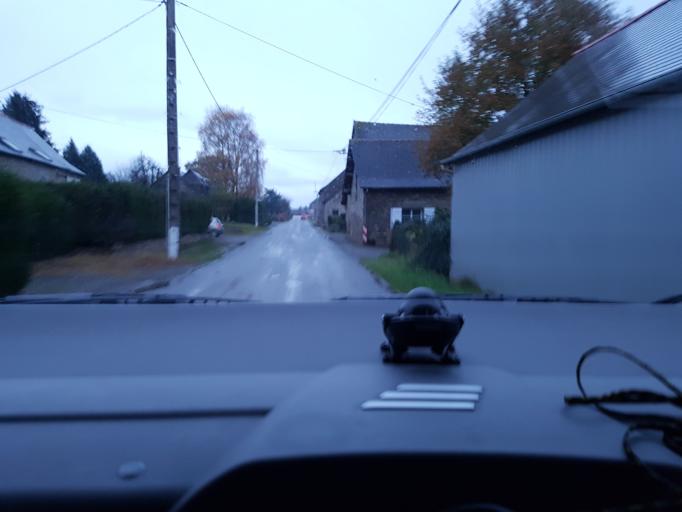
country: FR
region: Brittany
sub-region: Departement d'Ille-et-Vilaine
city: Livre-sur-Changeon
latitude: 48.2385
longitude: -1.3095
